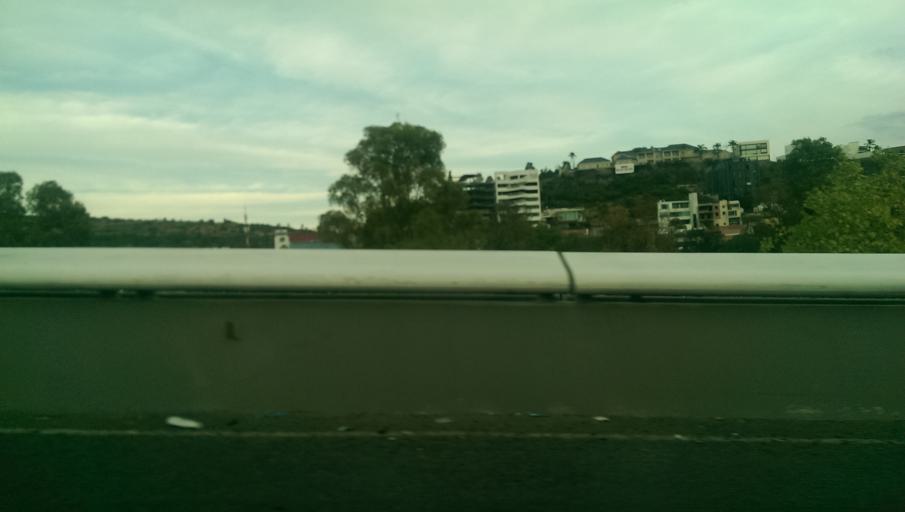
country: MX
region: Queretaro
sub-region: Queretaro
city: Santiago de Queretaro
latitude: 20.5879
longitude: -100.3634
